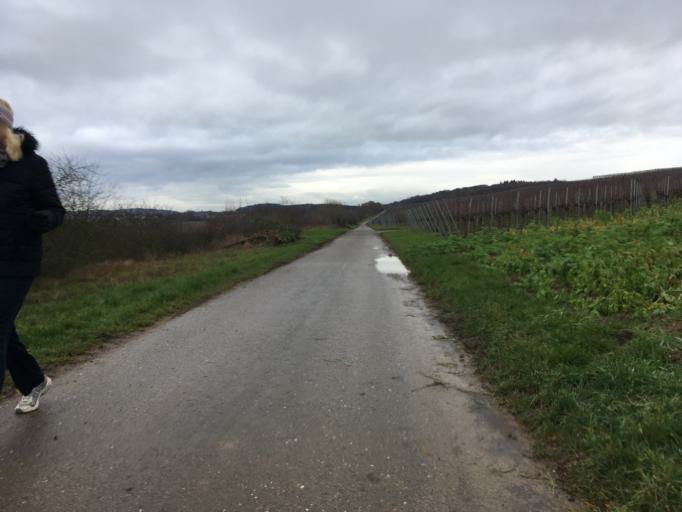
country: DE
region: Baden-Wuerttemberg
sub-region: Regierungsbezirk Stuttgart
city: Schwaigern
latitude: 49.1398
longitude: 9.0371
